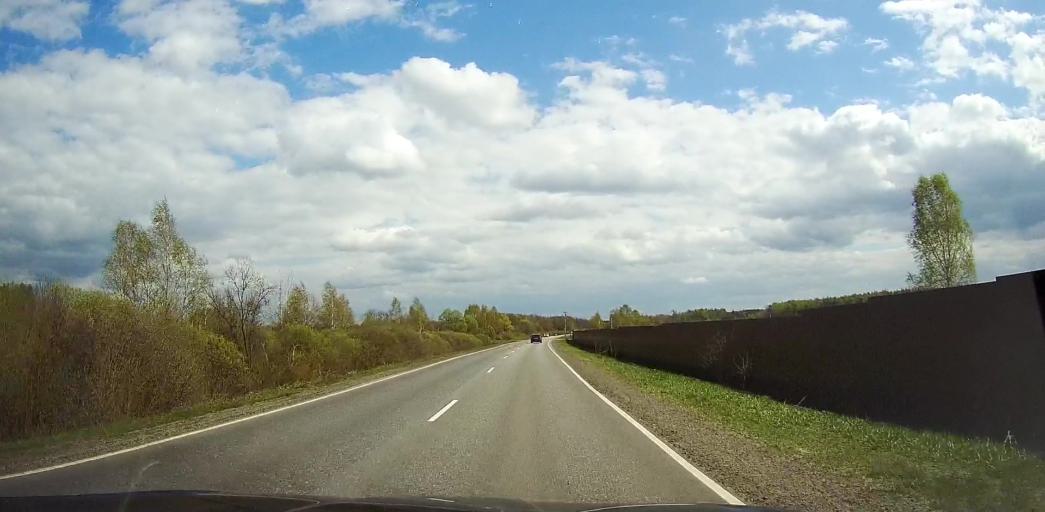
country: RU
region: Moskovskaya
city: Davydovo
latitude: 55.5512
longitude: 38.7907
